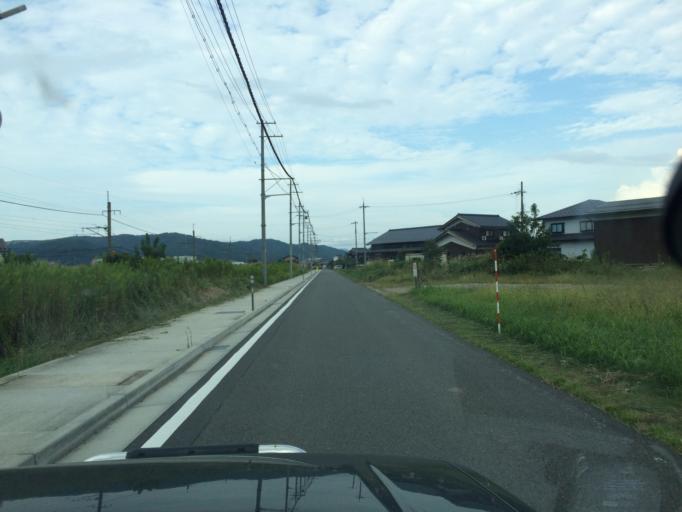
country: JP
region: Hyogo
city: Toyooka
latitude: 35.4753
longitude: 134.7811
